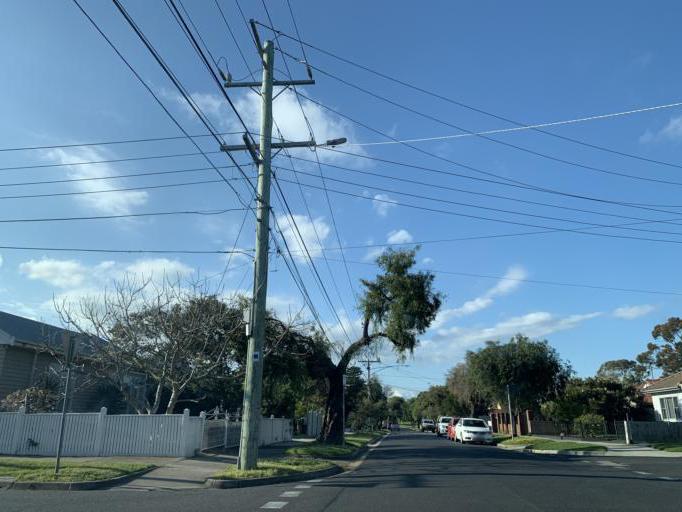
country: AU
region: Victoria
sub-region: Kingston
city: Mordialloc
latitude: -37.9944
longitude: 145.0883
